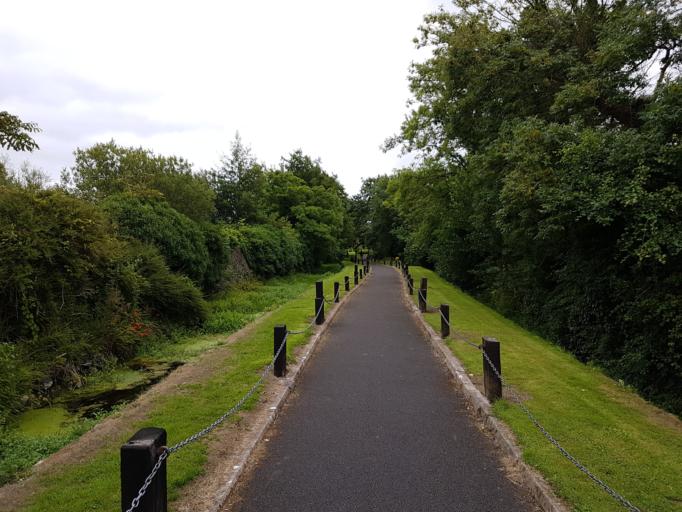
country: IE
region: Munster
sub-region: An Clar
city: Newmarket on Fergus
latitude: 52.7600
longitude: -8.8952
